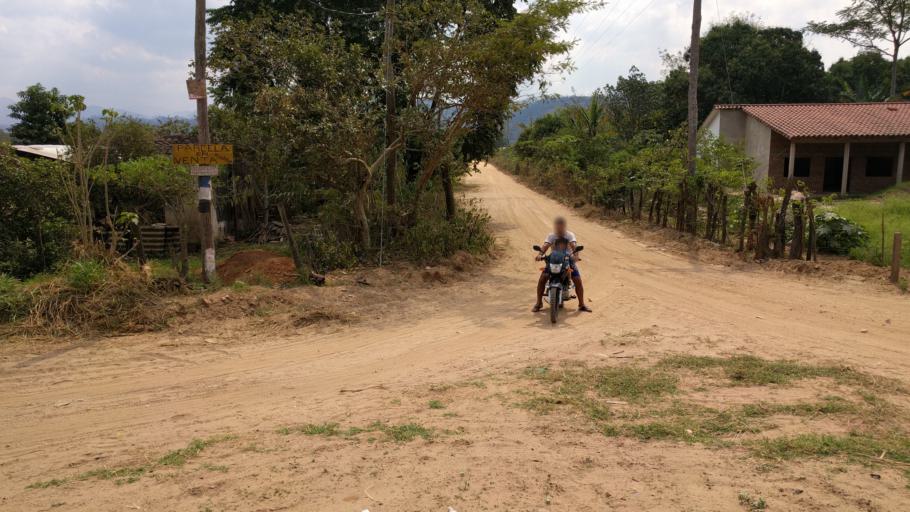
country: BO
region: Santa Cruz
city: Limoncito
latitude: -18.0430
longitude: -63.4151
